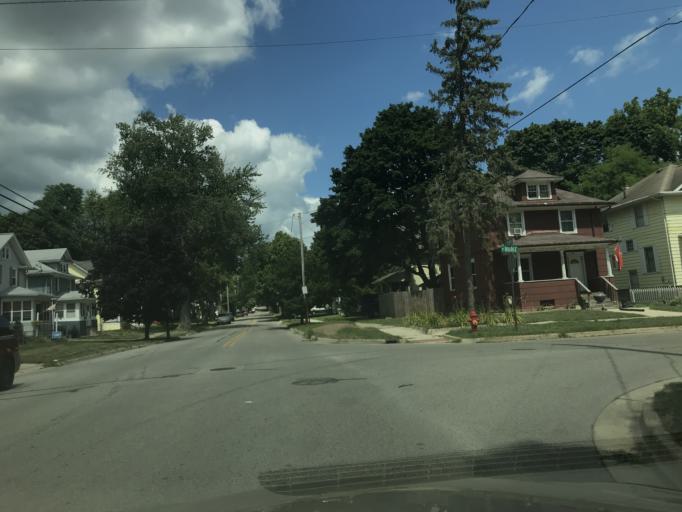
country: US
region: Michigan
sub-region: Jackson County
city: Jackson
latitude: 42.2412
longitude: -84.4185
